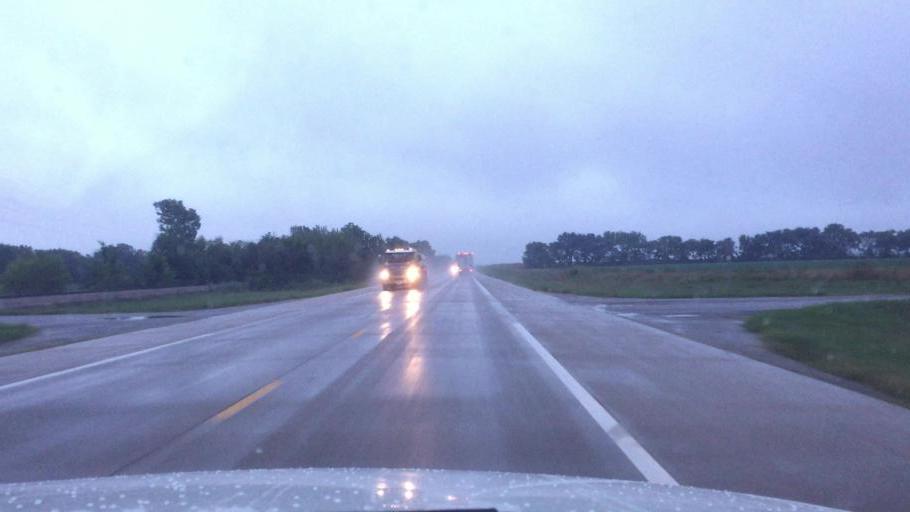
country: US
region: Kansas
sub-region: Neosho County
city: Chanute
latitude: 37.5437
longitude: -95.4708
